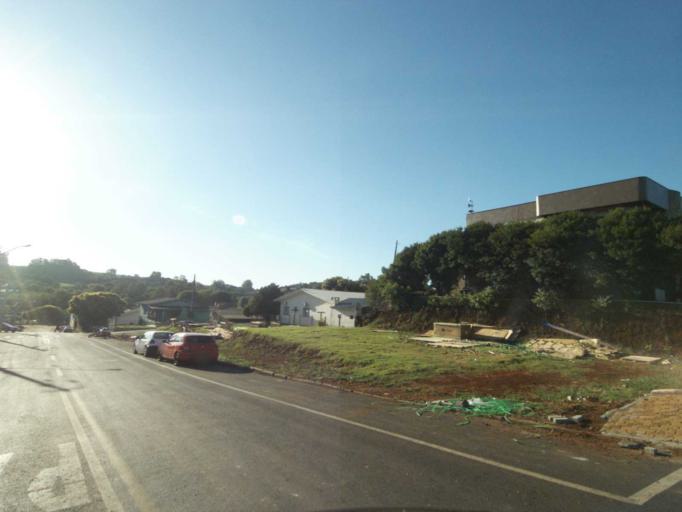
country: BR
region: Parana
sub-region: Coronel Vivida
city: Coronel Vivida
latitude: -25.9777
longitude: -52.8132
